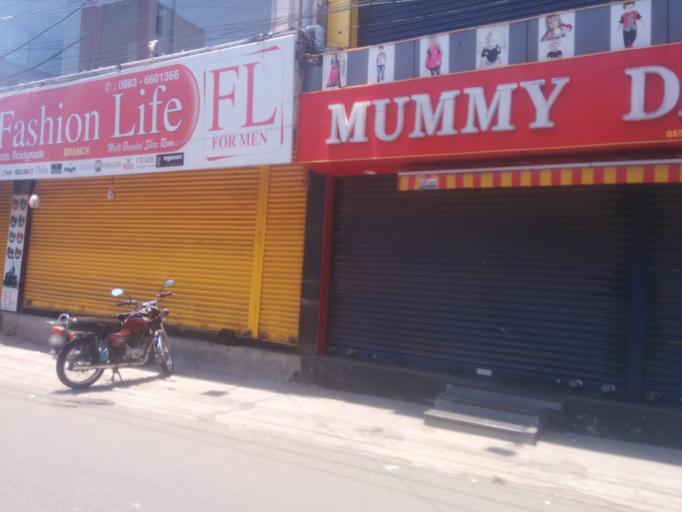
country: IN
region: Andhra Pradesh
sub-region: East Godavari
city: Rajahmundry
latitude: 17.0054
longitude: 81.7702
